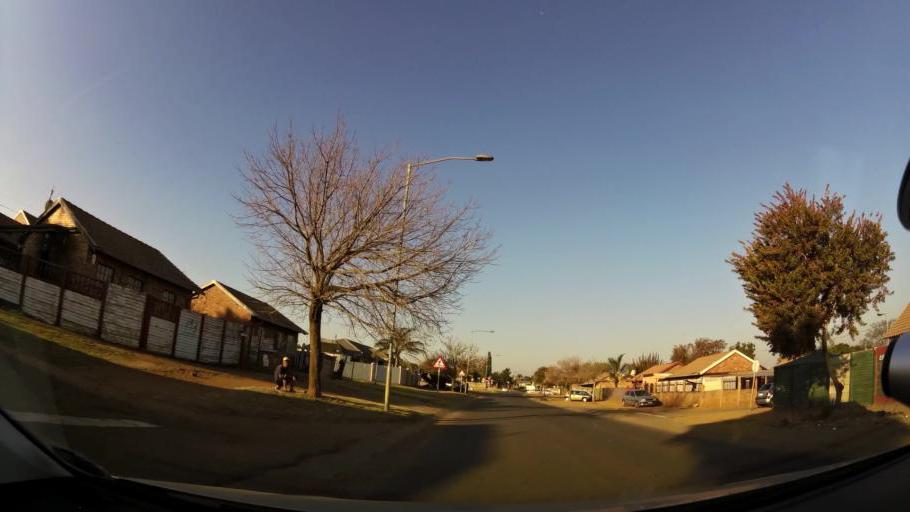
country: ZA
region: Gauteng
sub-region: City of Tshwane Metropolitan Municipality
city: Pretoria
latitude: -25.7385
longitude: 28.1159
